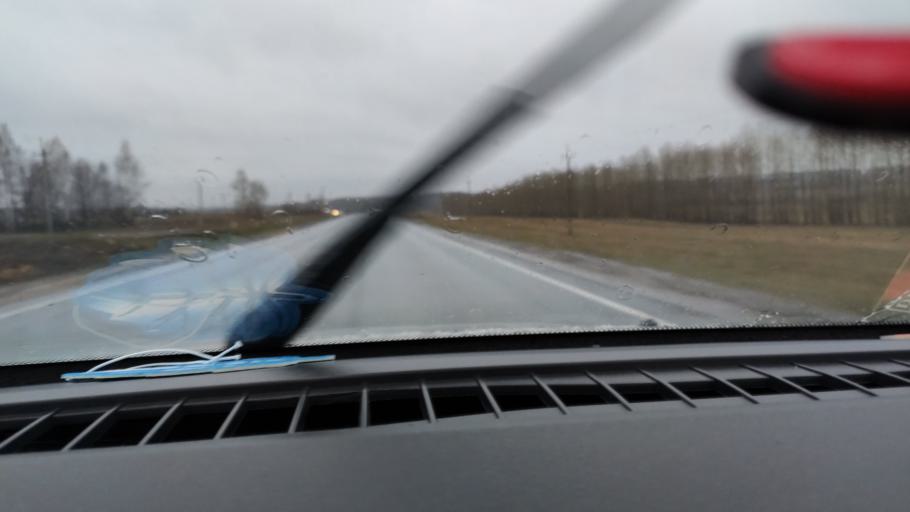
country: RU
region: Tatarstan
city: Mendeleyevsk
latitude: 55.9740
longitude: 52.3195
